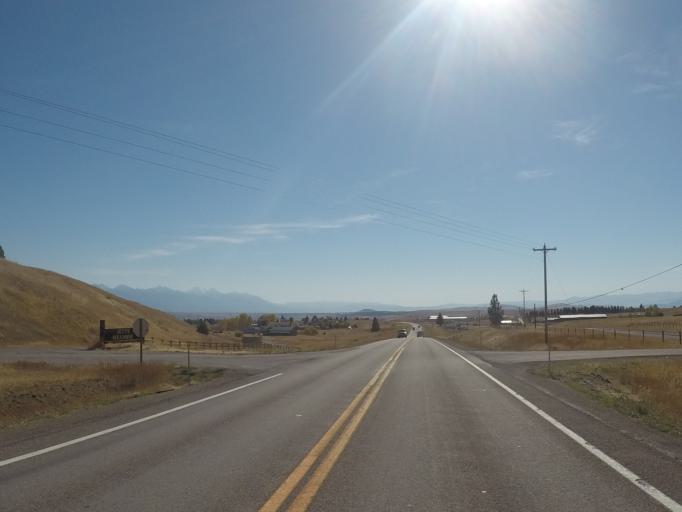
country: US
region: Montana
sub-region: Lake County
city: Polson
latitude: 47.7534
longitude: -114.2313
